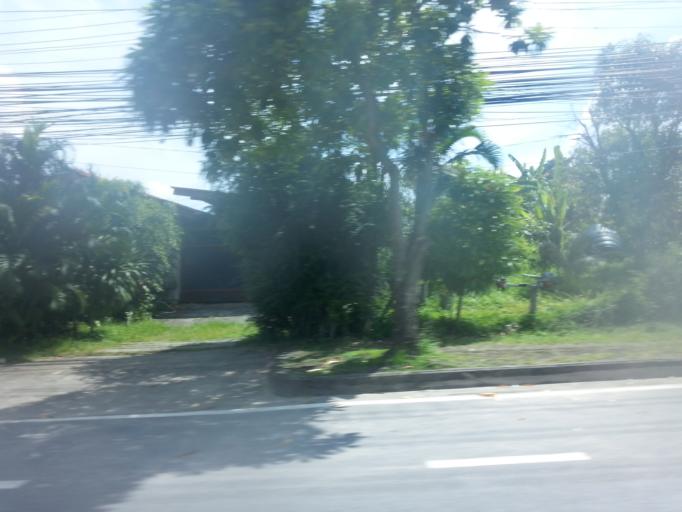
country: TH
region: Phuket
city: Kathu
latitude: 7.9080
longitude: 98.3306
